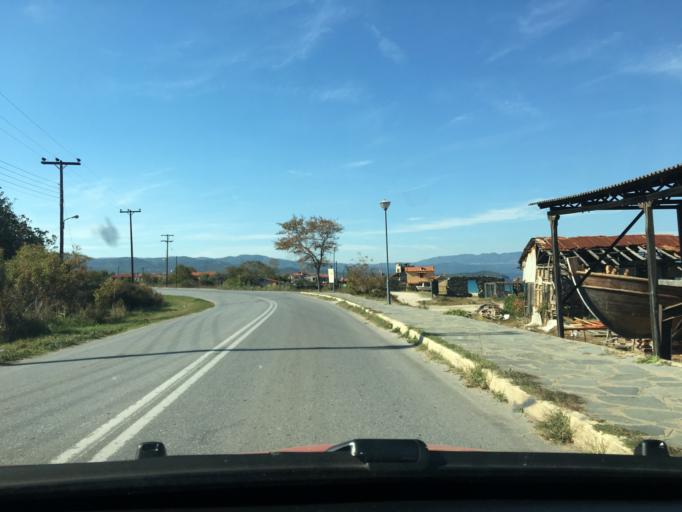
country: GR
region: Central Macedonia
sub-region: Nomos Chalkidikis
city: Ierissos
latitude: 40.3959
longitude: 23.8872
